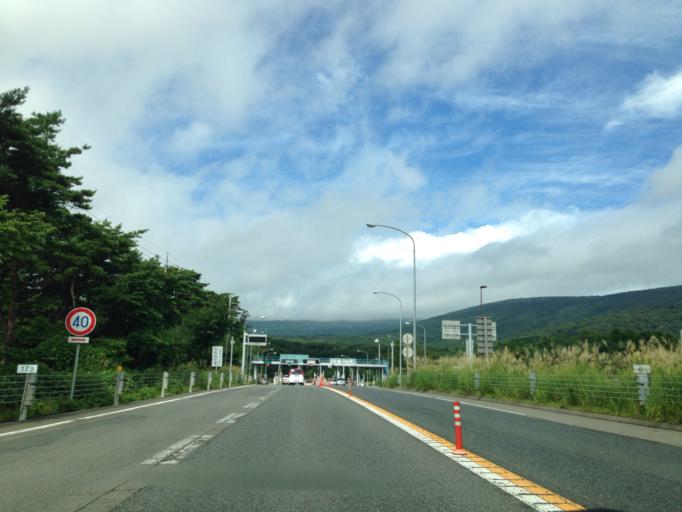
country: JP
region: Shizuoka
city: Gotemba
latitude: 35.3623
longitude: 138.8566
